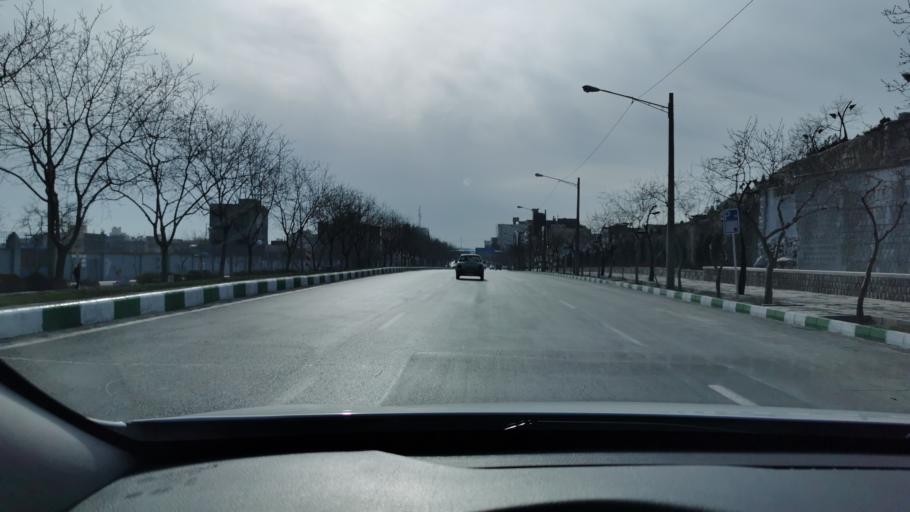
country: IR
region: Razavi Khorasan
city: Mashhad
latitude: 36.2948
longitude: 59.5314
